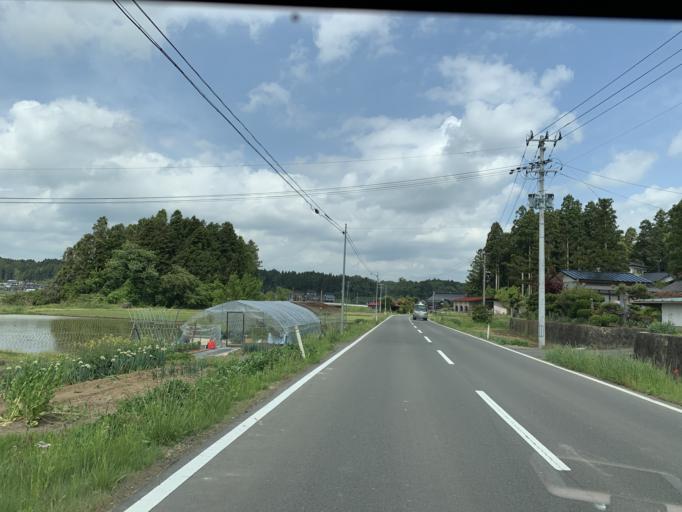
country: JP
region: Iwate
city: Ichinoseki
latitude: 38.8336
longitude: 141.0196
